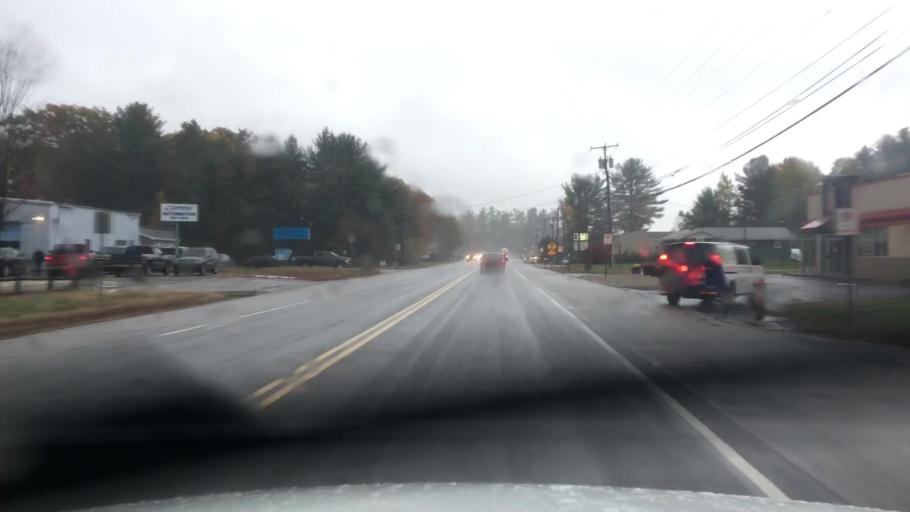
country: US
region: New Hampshire
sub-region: Strafford County
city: Rochester
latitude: 43.2577
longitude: -70.9791
